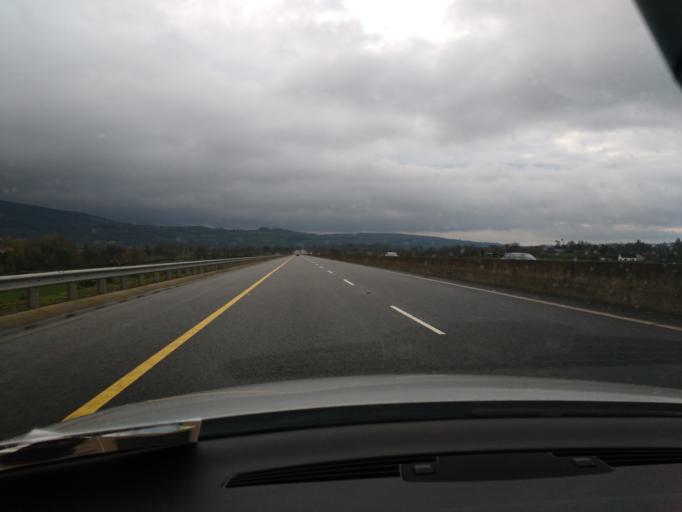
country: IE
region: Munster
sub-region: North Tipperary
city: Nenagh
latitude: 52.8183
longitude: -8.3063
